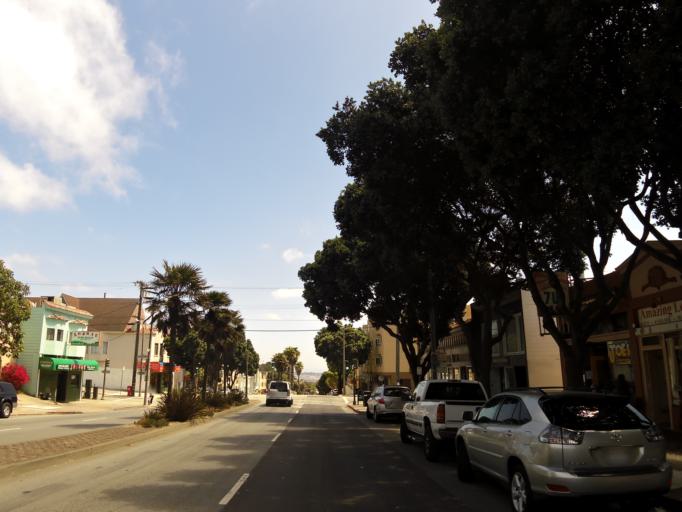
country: US
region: California
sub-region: San Mateo County
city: Daly City
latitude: 37.7315
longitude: -122.4517
